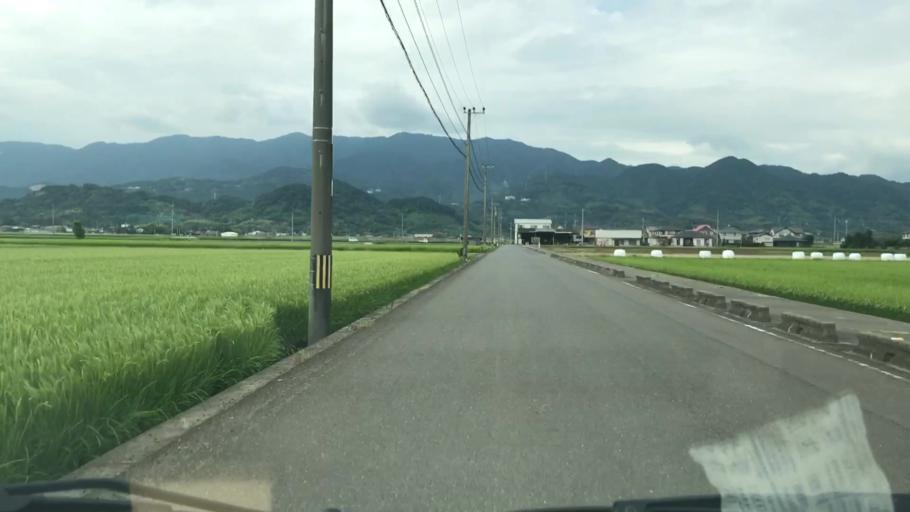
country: JP
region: Saga Prefecture
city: Saga-shi
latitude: 33.2864
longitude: 130.2252
